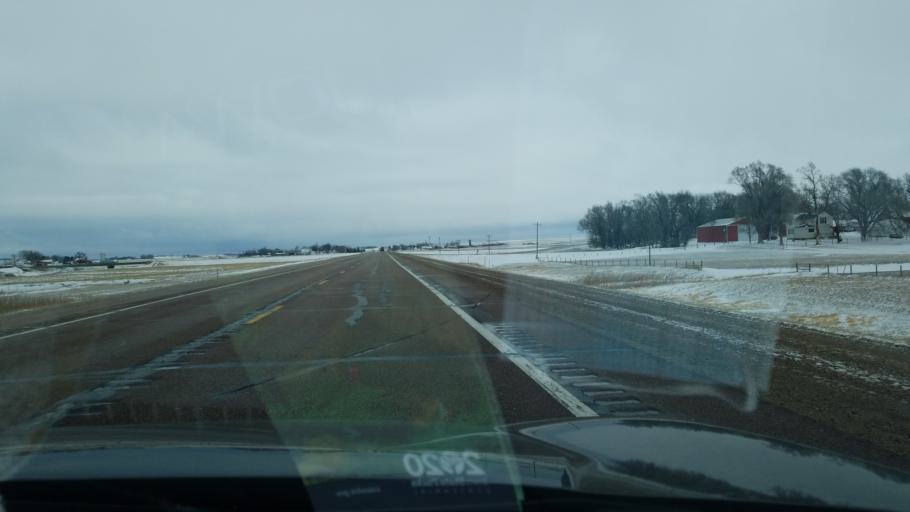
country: US
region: Iowa
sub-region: Plymouth County
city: Le Mars
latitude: 42.9196
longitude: -96.1750
